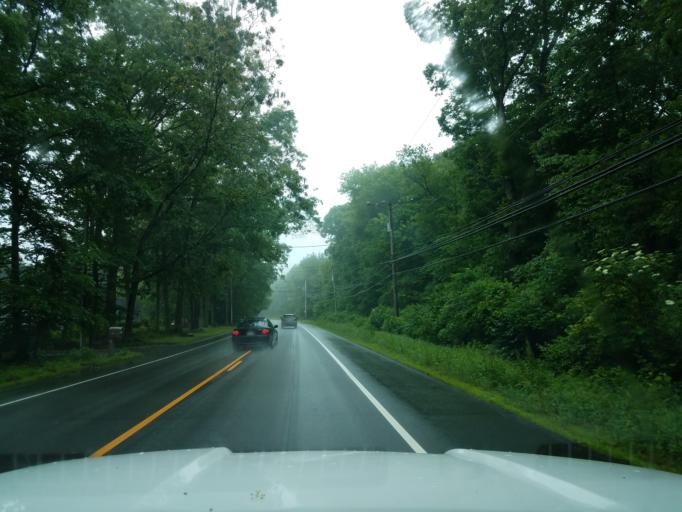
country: US
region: Connecticut
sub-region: New Haven County
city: Madison Center
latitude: 41.3325
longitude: -72.6243
